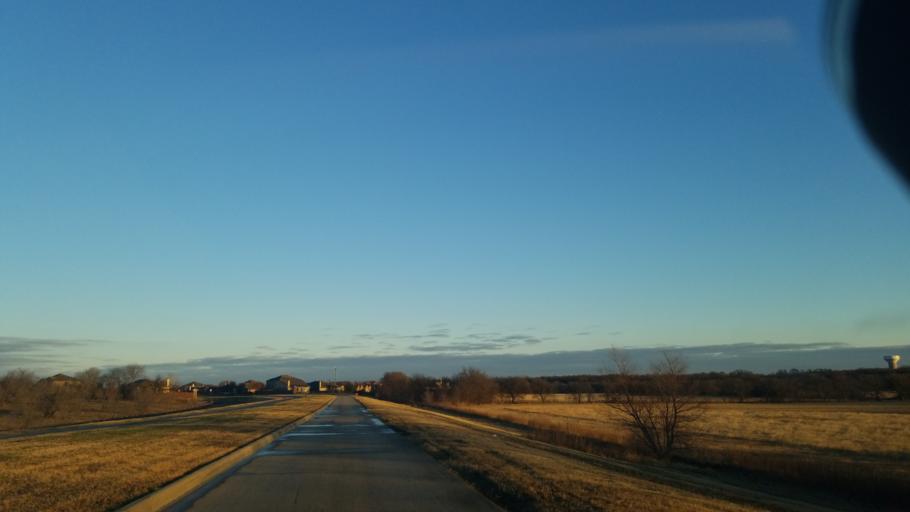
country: US
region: Texas
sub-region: Denton County
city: Argyle
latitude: 33.1665
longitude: -97.1591
